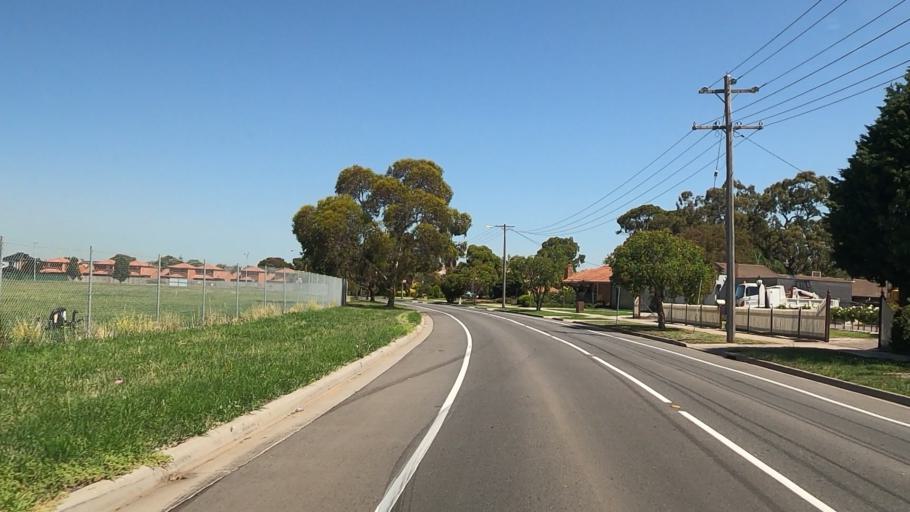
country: AU
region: Victoria
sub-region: Hume
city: Attwood
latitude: -37.6494
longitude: 144.8894
